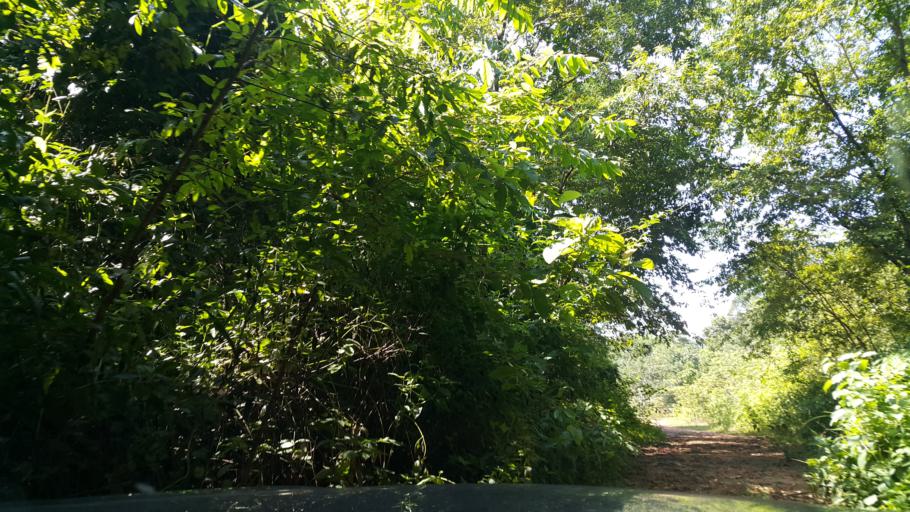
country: TH
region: Chiang Mai
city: San Sai
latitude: 18.9553
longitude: 99.1386
